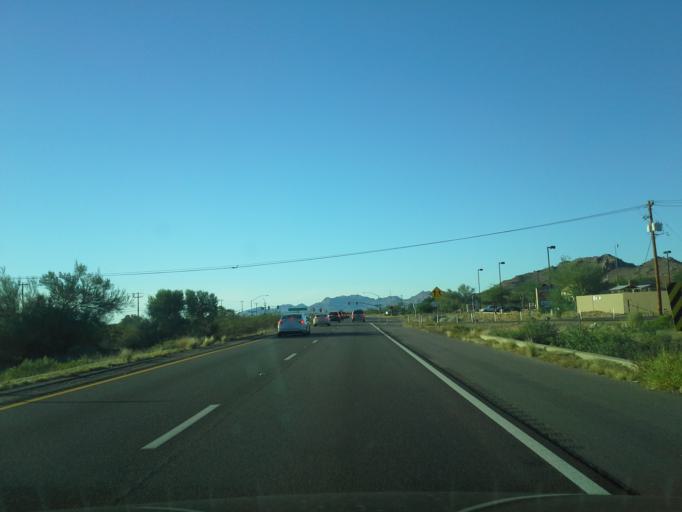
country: US
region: Arizona
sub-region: Pinal County
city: Apache Junction
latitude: 33.3647
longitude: -111.4758
